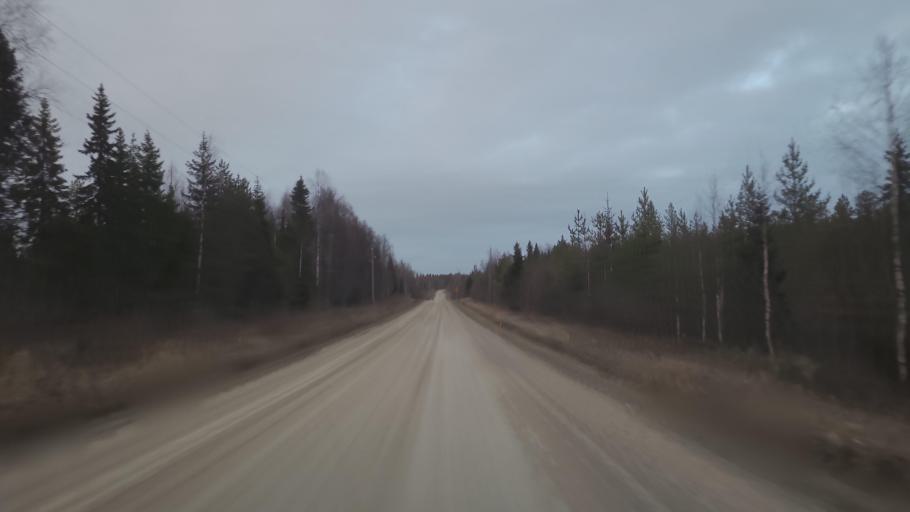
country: FI
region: Lapland
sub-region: Kemi-Tornio
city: Tervola
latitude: 66.0689
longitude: 25.0808
